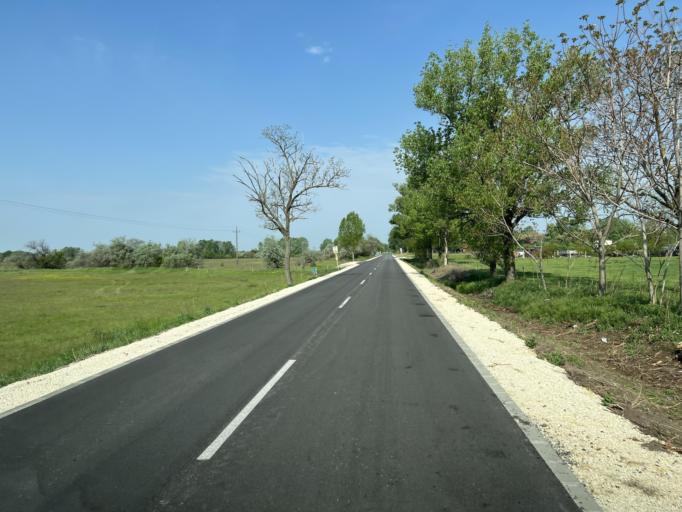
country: HU
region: Pest
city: Kocser
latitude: 46.9953
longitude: 19.9471
